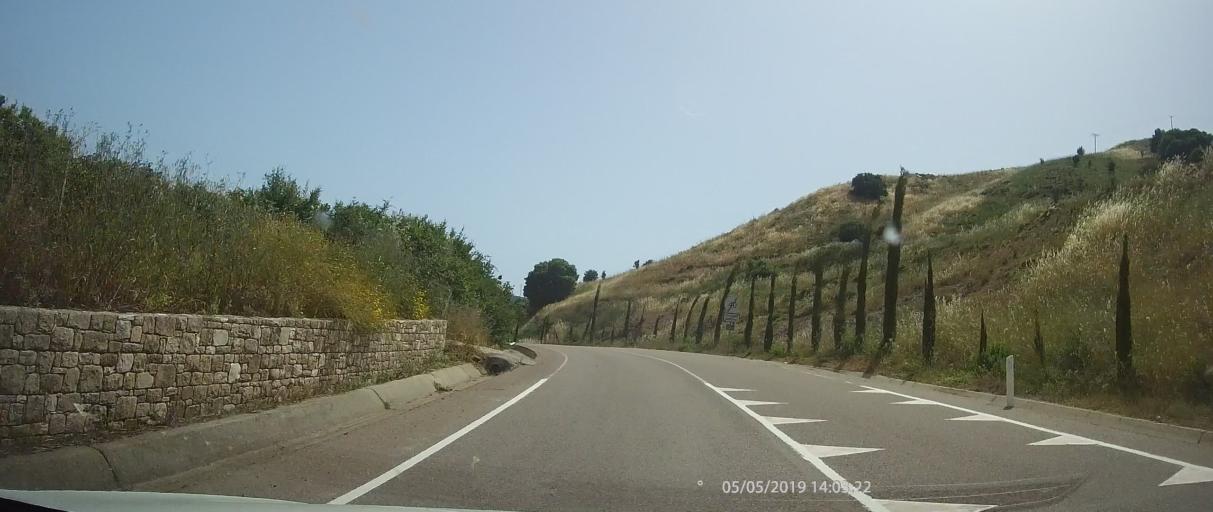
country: CY
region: Limassol
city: Pissouri
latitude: 34.7692
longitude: 32.6350
